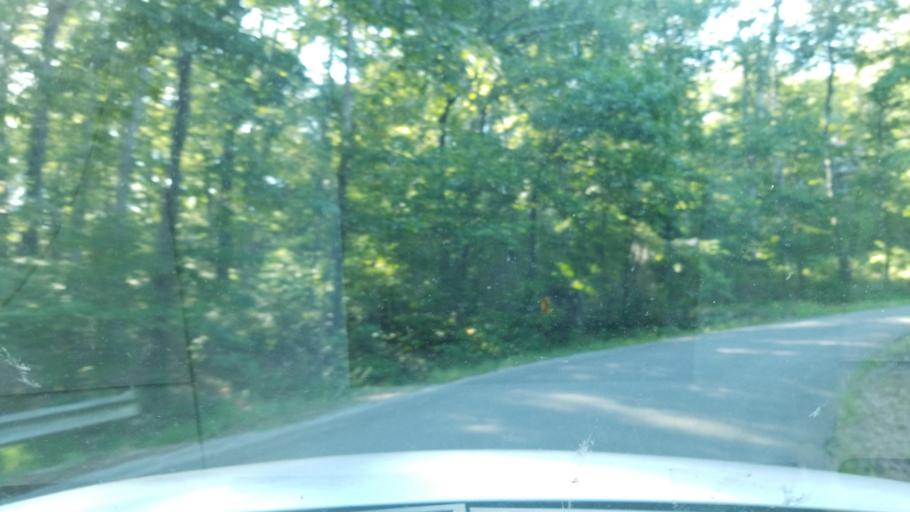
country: US
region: Illinois
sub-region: Hardin County
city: Elizabethtown
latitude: 37.6026
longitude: -88.3839
